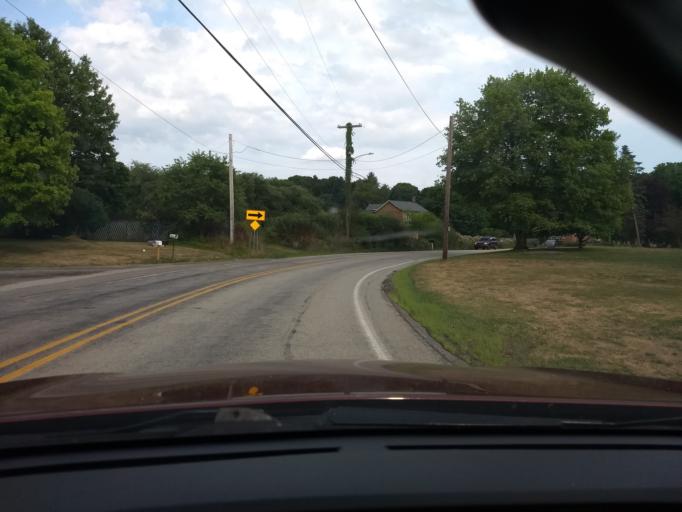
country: US
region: Pennsylvania
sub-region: Allegheny County
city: Curtisville
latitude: 40.6595
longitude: -79.8446
